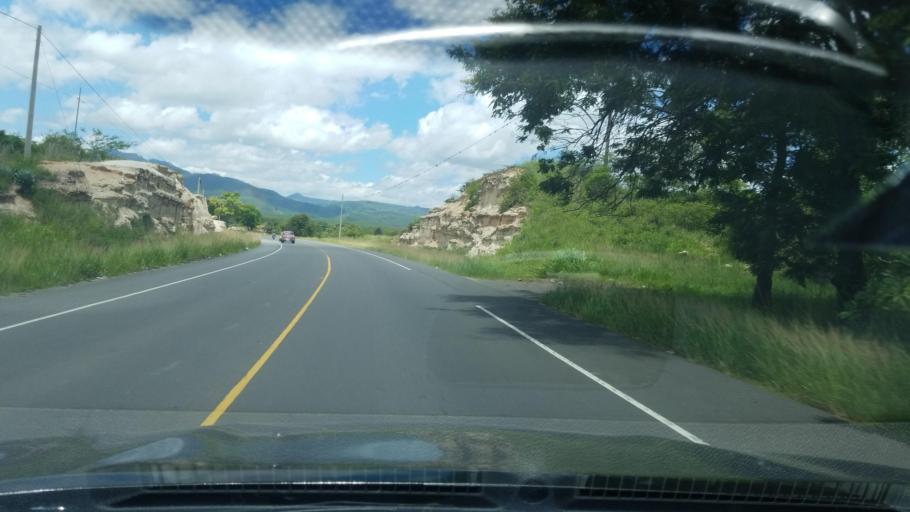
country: HN
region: Francisco Morazan
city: Cofradia
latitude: 14.2931
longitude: -87.2427
